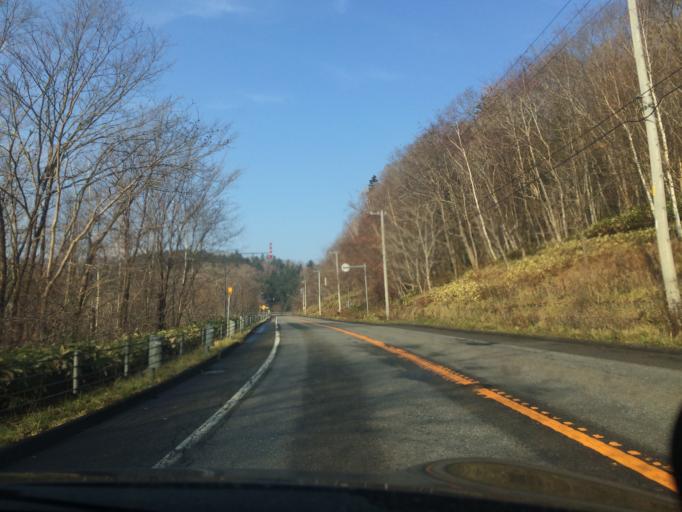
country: JP
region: Hokkaido
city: Shimo-furano
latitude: 42.8920
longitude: 142.2482
